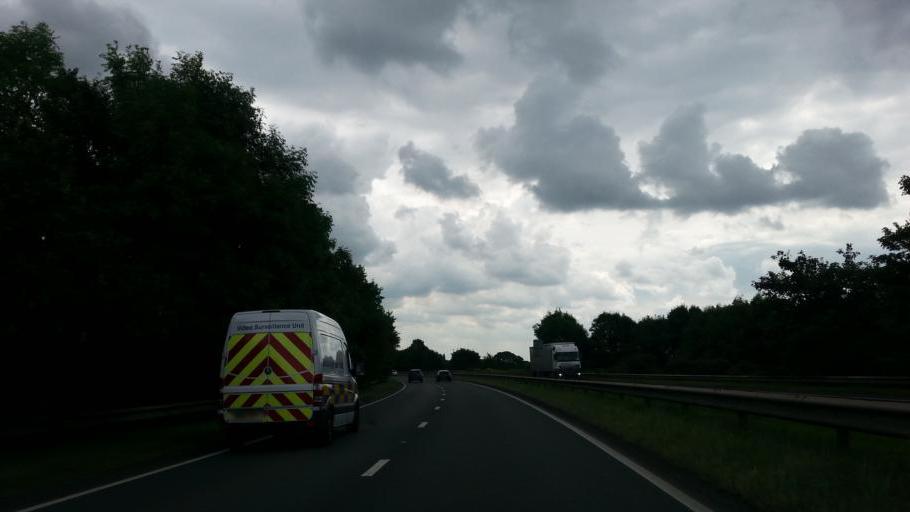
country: GB
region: England
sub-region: City and Borough of Birmingham
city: Sutton Coldfield
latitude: 52.5966
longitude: -1.7942
